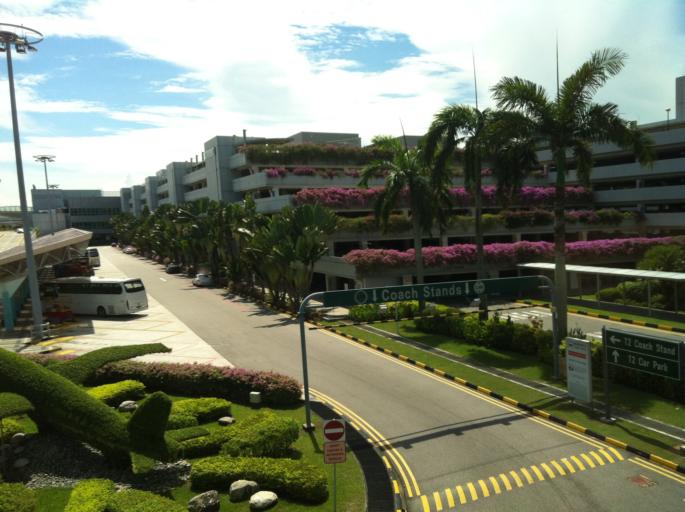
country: SG
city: Singapore
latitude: 1.3518
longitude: 103.9869
